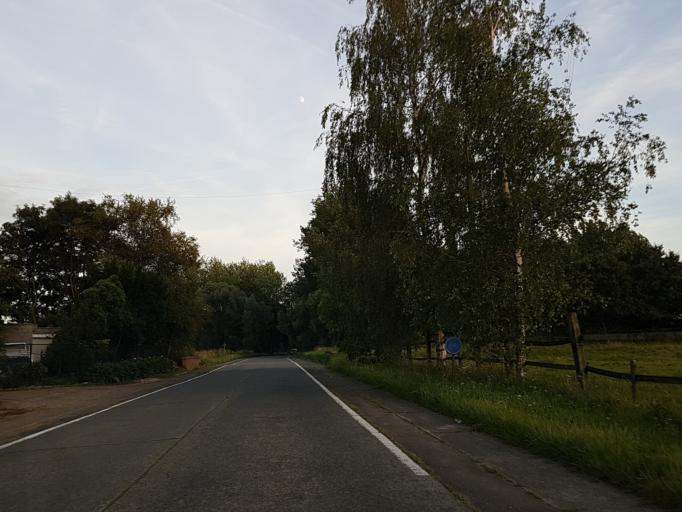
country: BE
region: Flanders
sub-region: Provincie Vlaams-Brabant
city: Londerzeel
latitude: 50.9856
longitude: 4.2672
